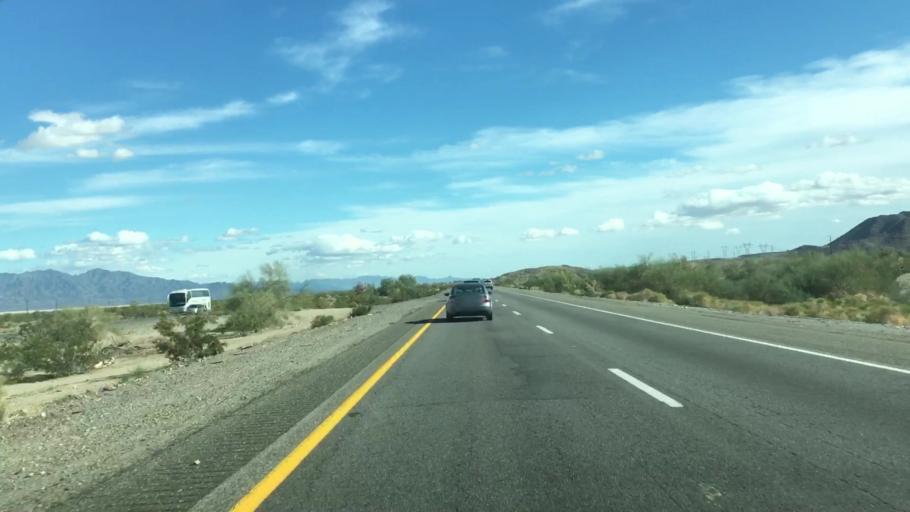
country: US
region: California
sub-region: Imperial County
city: Niland
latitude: 33.7086
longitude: -115.3648
